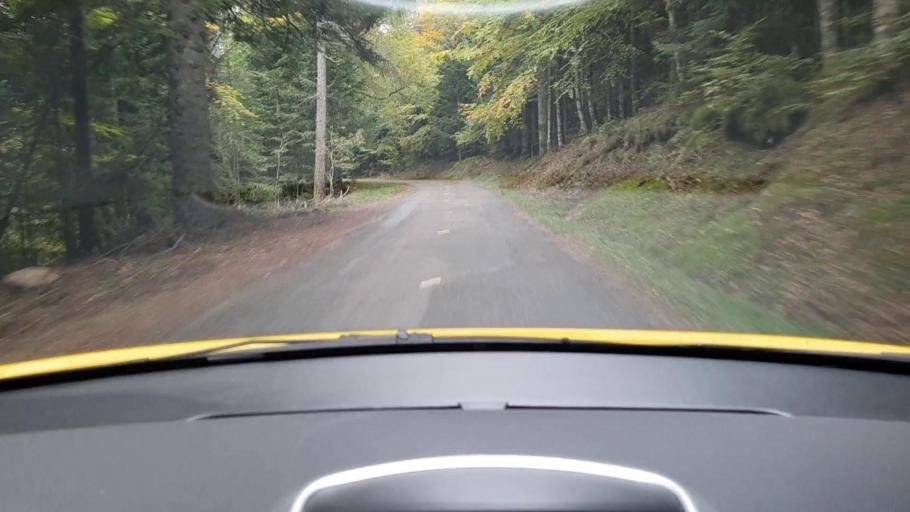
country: FR
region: Languedoc-Roussillon
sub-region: Departement de la Lozere
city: Meyrueis
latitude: 44.1010
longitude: 3.4758
